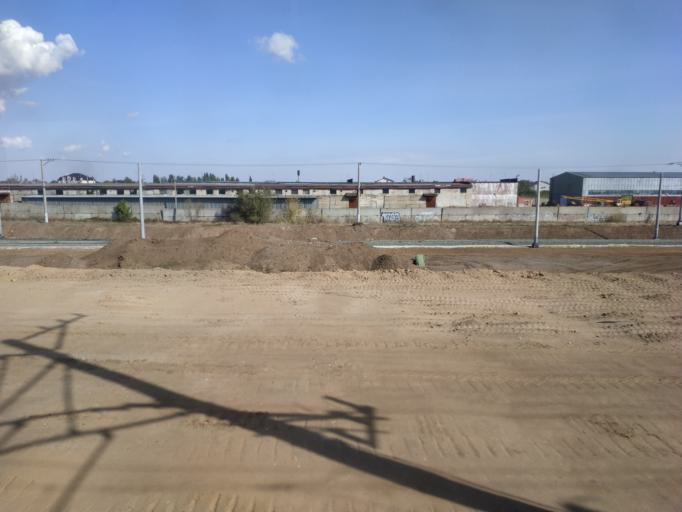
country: RU
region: Volgograd
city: Gumrak
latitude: 48.7720
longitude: 44.3864
